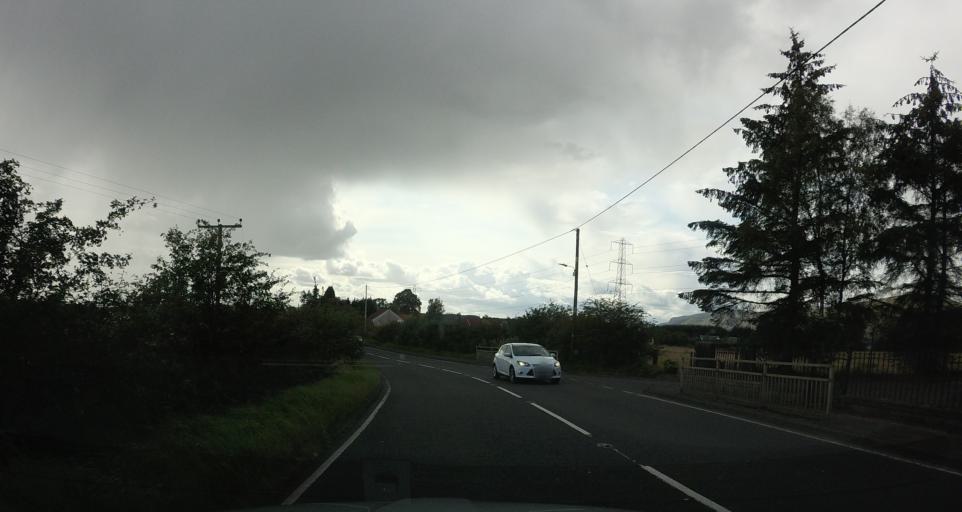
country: GB
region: Scotland
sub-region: Clackmannanshire
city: Dollar
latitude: 56.1548
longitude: -3.6313
